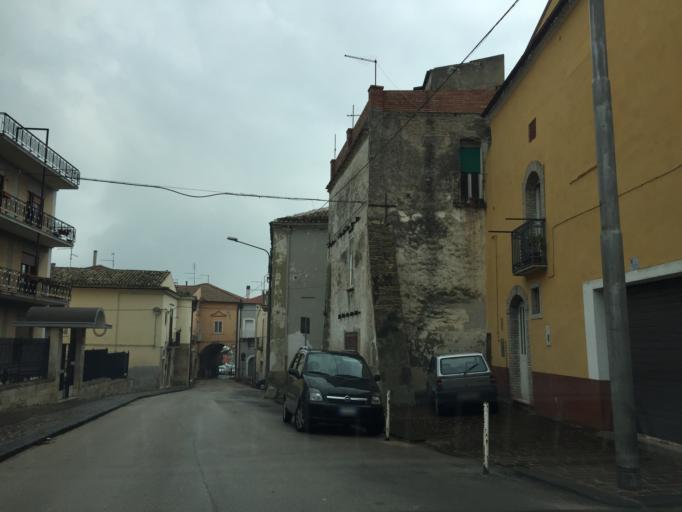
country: IT
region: Apulia
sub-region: Provincia di Foggia
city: Troia
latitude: 41.3611
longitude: 15.3067
